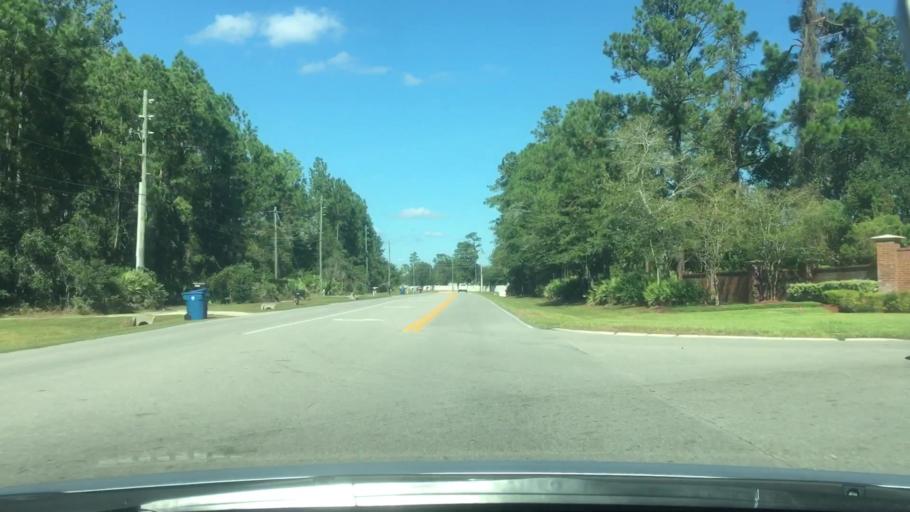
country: US
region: Florida
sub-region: Nassau County
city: Yulee
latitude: 30.4865
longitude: -81.5759
